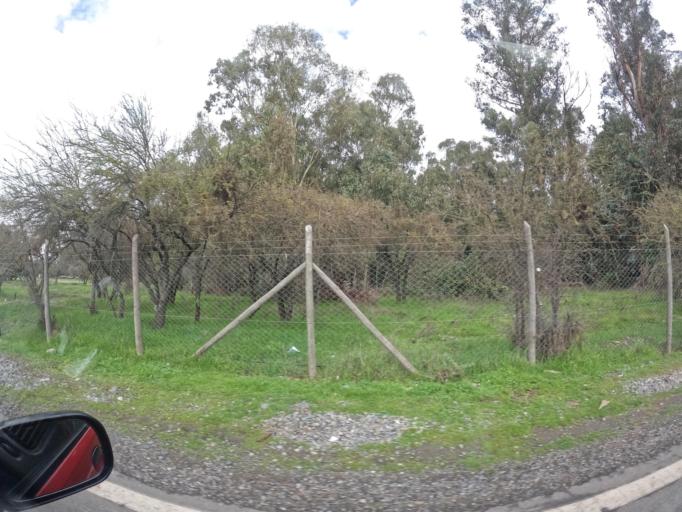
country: CL
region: Maule
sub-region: Provincia de Linares
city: Linares
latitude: -35.8669
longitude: -71.6299
